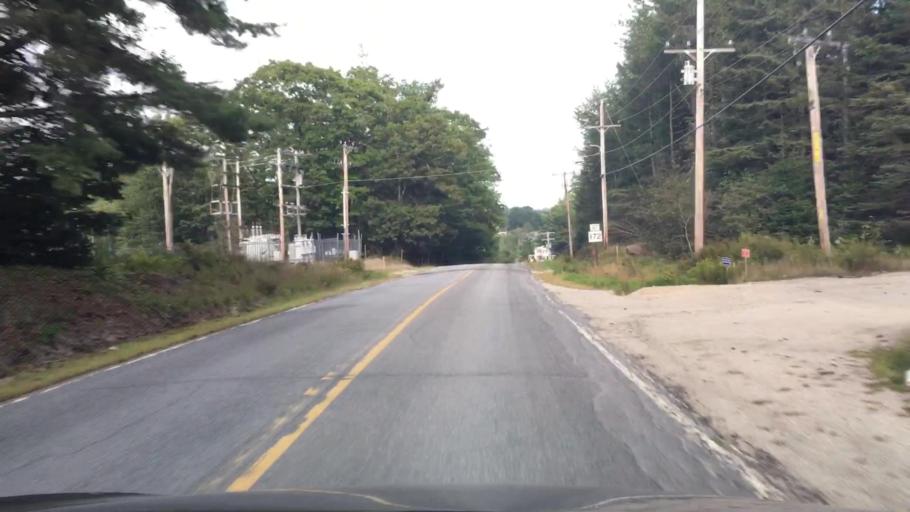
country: US
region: Maine
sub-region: Hancock County
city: Surry
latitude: 44.4940
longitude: -68.5100
